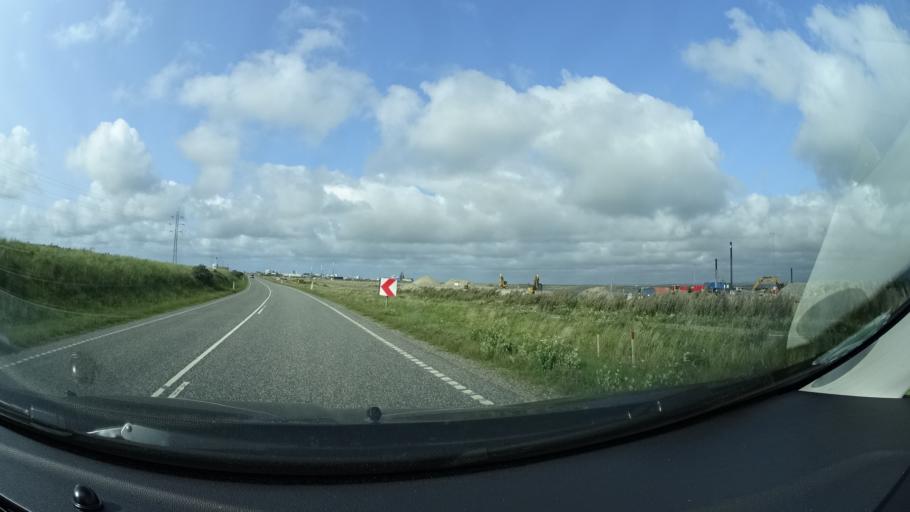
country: DK
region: Central Jutland
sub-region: Lemvig Kommune
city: Thyboron
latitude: 56.6828
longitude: 8.2240
